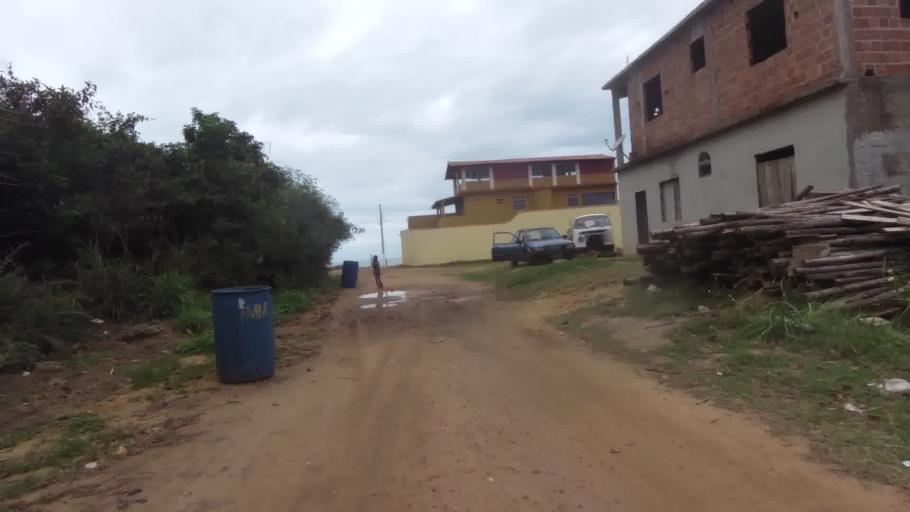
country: BR
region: Espirito Santo
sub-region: Marataizes
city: Marataizes
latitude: -21.0616
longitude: -40.8356
